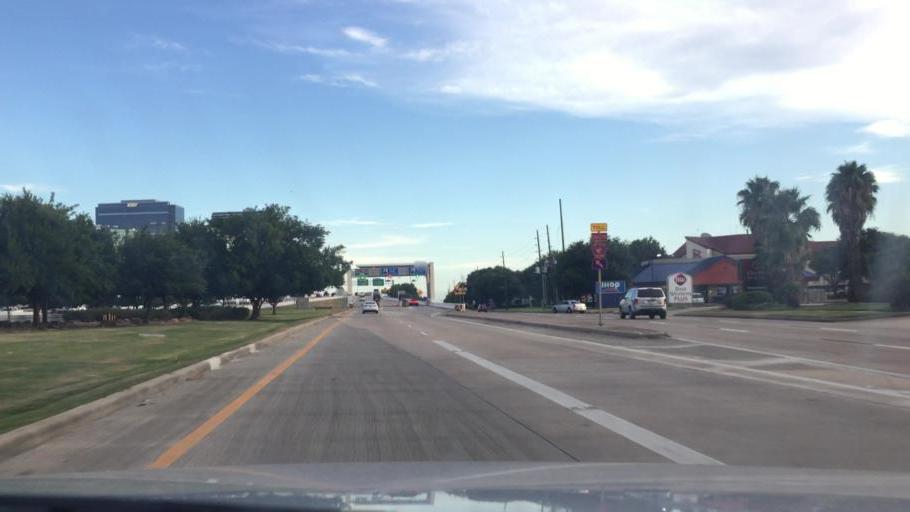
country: US
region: Texas
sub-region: Harris County
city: Bunker Hill Village
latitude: 29.7342
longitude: -95.5582
